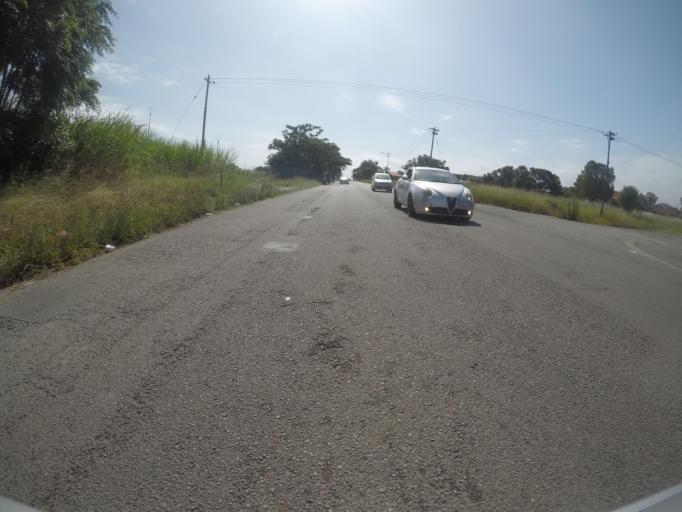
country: ZA
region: Eastern Cape
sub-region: Buffalo City Metropolitan Municipality
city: East London
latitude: -32.9709
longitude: 27.8775
